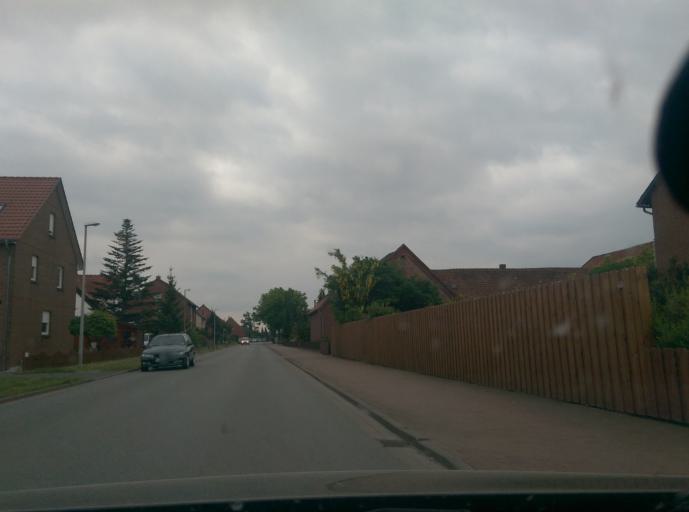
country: DE
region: Lower Saxony
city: Garbsen-Mitte
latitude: 52.4606
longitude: 9.6035
